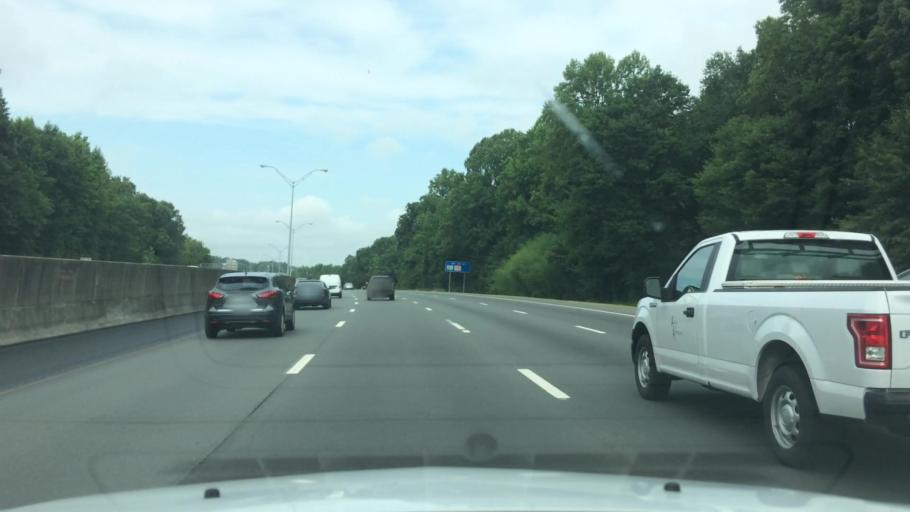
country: US
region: North Carolina
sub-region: Alamance County
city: Elon
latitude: 36.0695
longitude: -79.4852
